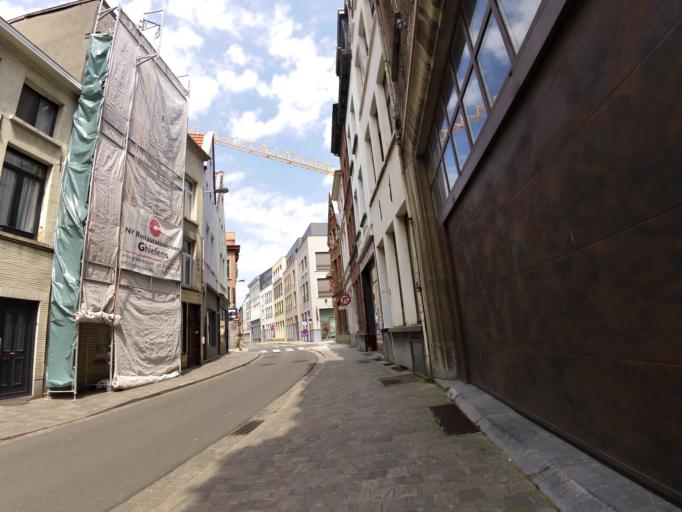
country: BE
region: Flanders
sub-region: Provincie Antwerpen
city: Antwerpen
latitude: 51.2218
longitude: 4.4111
